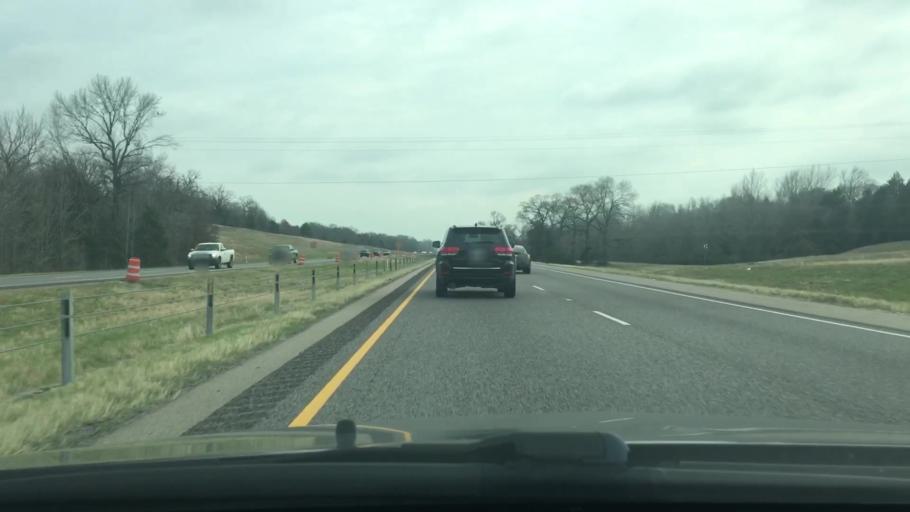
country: US
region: Texas
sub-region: Leon County
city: Buffalo
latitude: 31.4989
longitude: -96.0969
